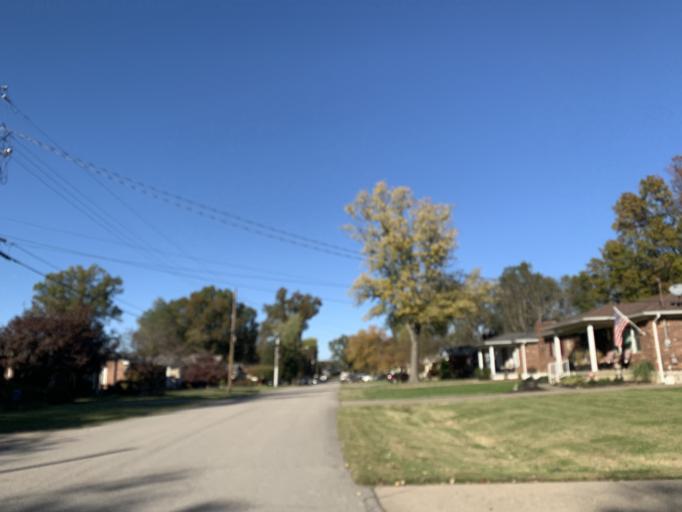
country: US
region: Kentucky
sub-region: Jefferson County
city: Pleasure Ridge Park
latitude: 38.1604
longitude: -85.8646
